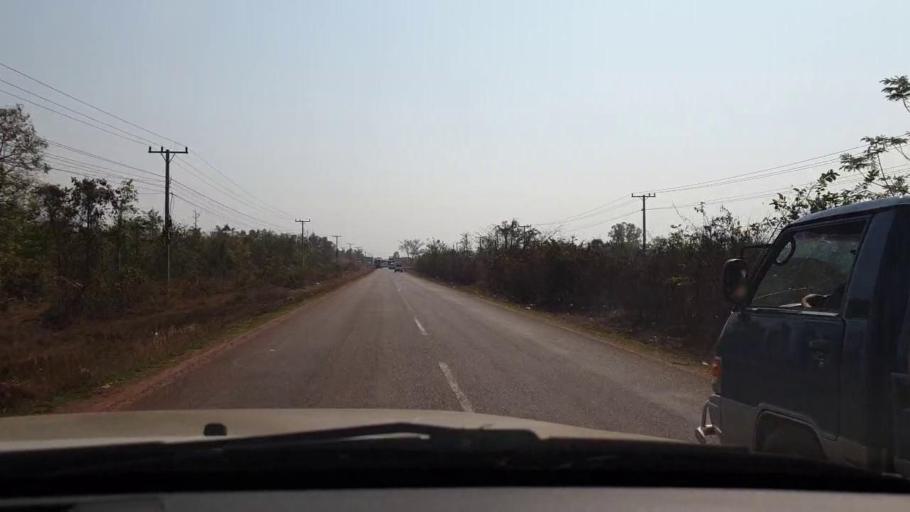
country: TH
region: Nong Khai
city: Nong Khai
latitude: 18.0538
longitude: 102.8401
